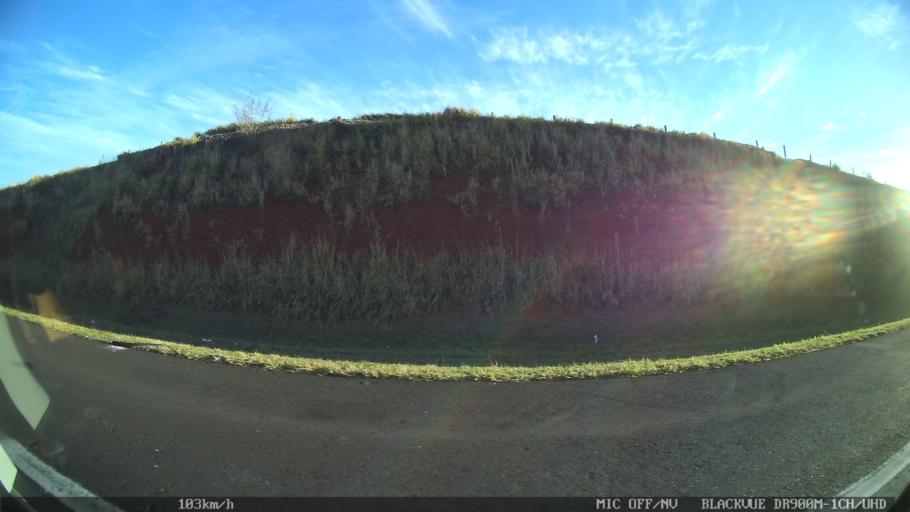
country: BR
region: Sao Paulo
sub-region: Catanduva
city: Catanduva
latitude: -21.0521
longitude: -49.1267
